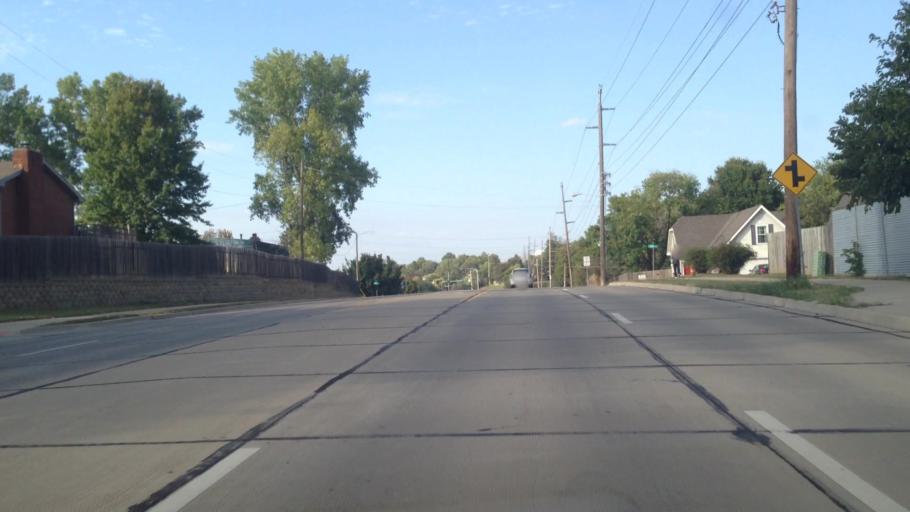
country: US
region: Kansas
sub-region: Douglas County
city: Lawrence
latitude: 38.9396
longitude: -95.2791
